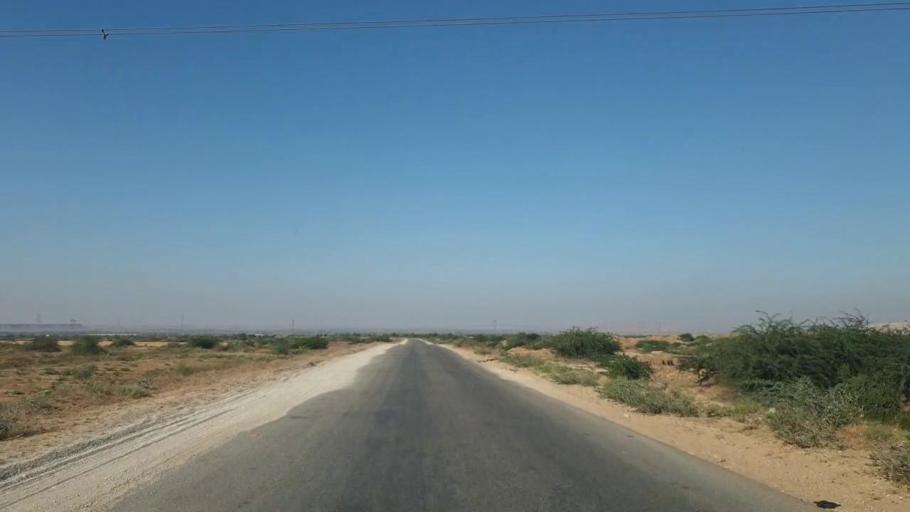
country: PK
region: Sindh
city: Gharo
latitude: 25.1631
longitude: 67.6627
